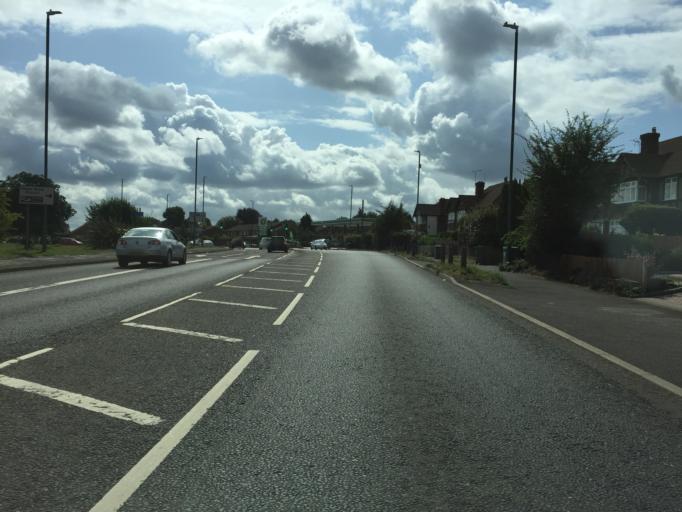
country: GB
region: England
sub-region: Kent
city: Aylesford
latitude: 51.2858
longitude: 0.4934
